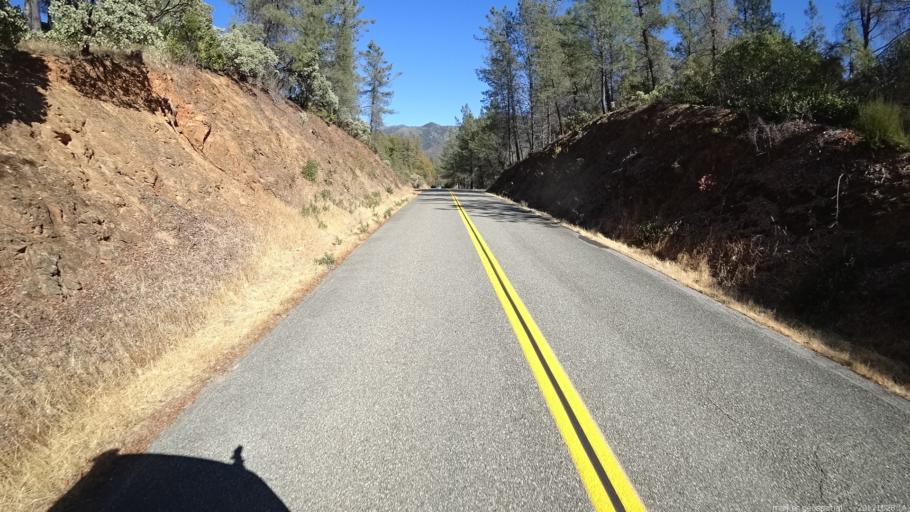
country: US
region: California
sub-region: Shasta County
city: Shasta
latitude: 40.6385
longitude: -122.5598
